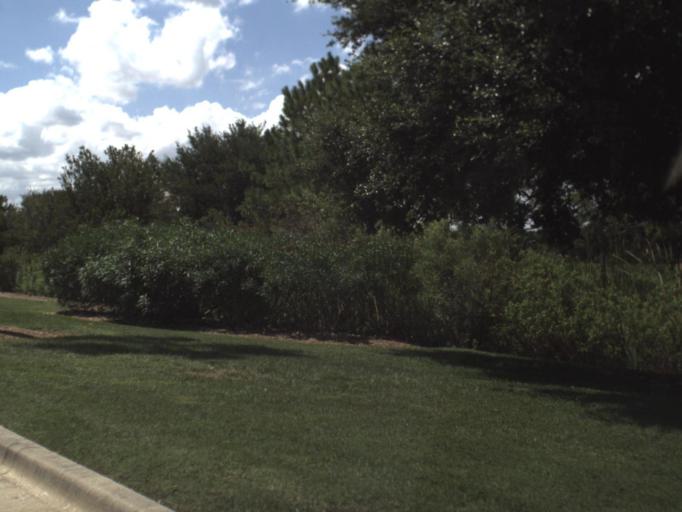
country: US
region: Florida
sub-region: Hillsborough County
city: Brandon
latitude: 27.9285
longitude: -82.3047
